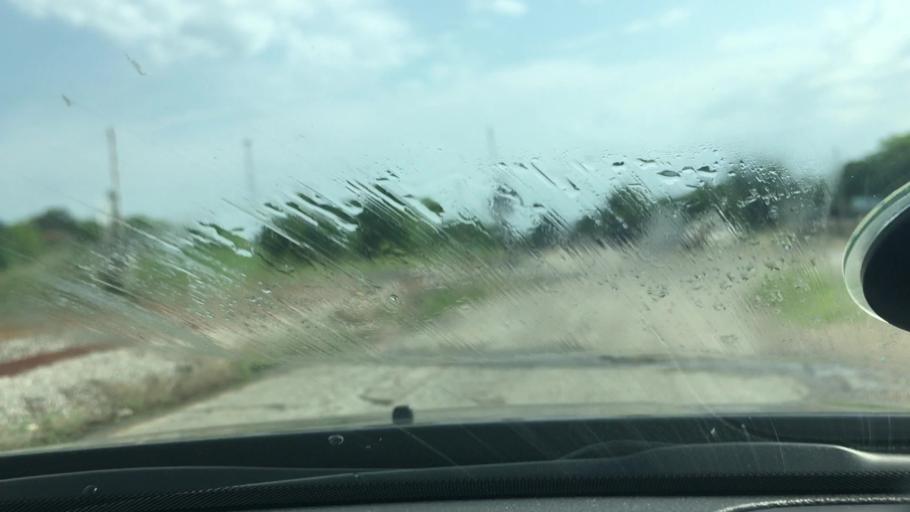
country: US
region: Oklahoma
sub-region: Atoka County
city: Atoka
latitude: 34.4664
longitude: -96.0566
